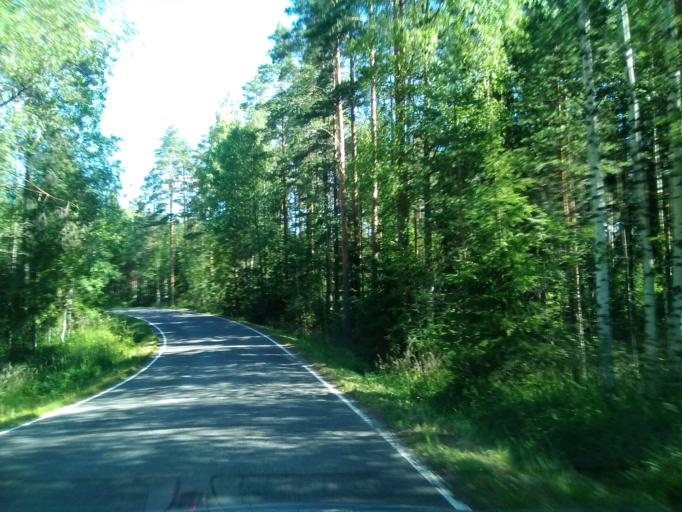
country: FI
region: Uusimaa
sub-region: Helsinki
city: Kaerkoelae
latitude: 60.7849
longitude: 24.0809
